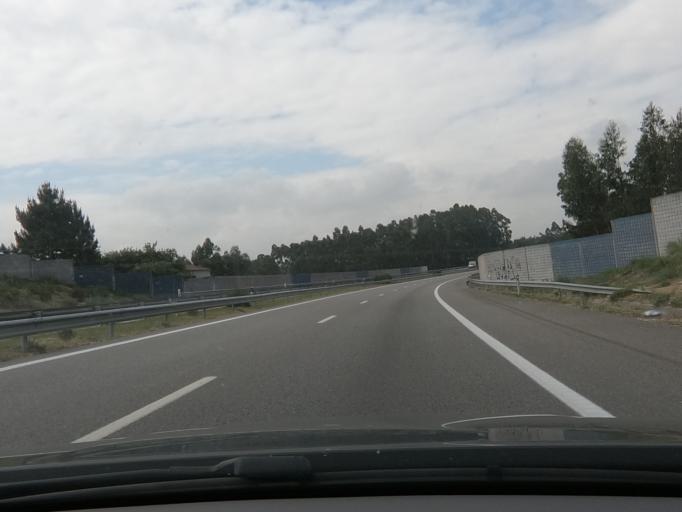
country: PT
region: Aveiro
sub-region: Aveiro
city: Oliveirinha
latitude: 40.6088
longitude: -8.5848
